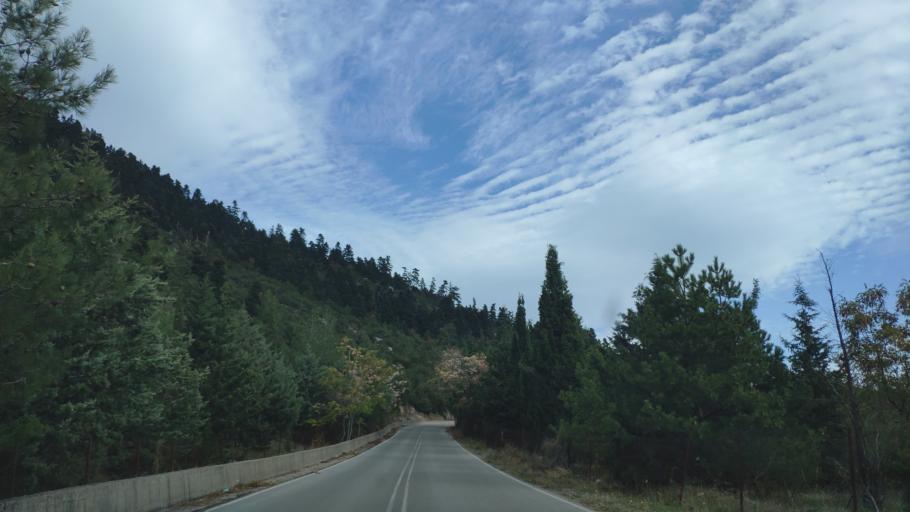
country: GR
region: Central Greece
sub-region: Nomos Fokidos
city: Amfissa
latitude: 38.6354
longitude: 22.3805
